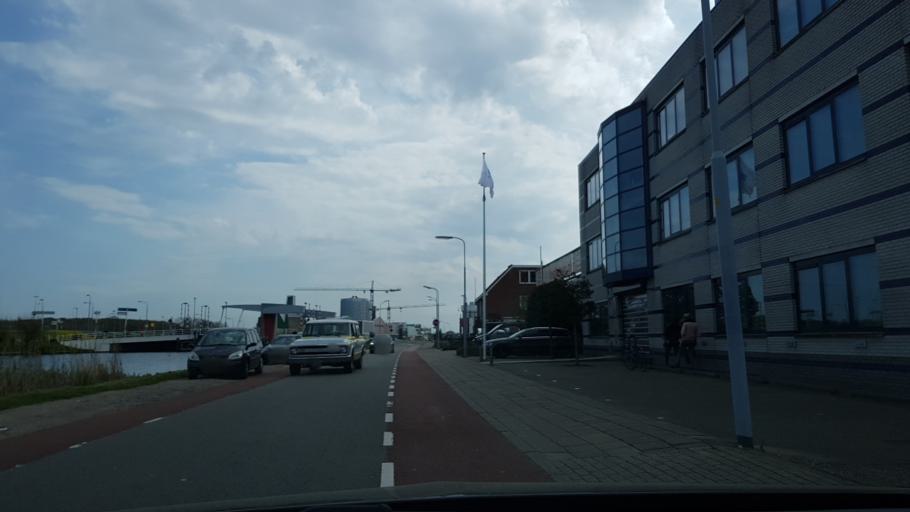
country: NL
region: North Holland
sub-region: Gemeente Haarlemmermeer
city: Hoofddorp
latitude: 52.3860
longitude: 4.7317
